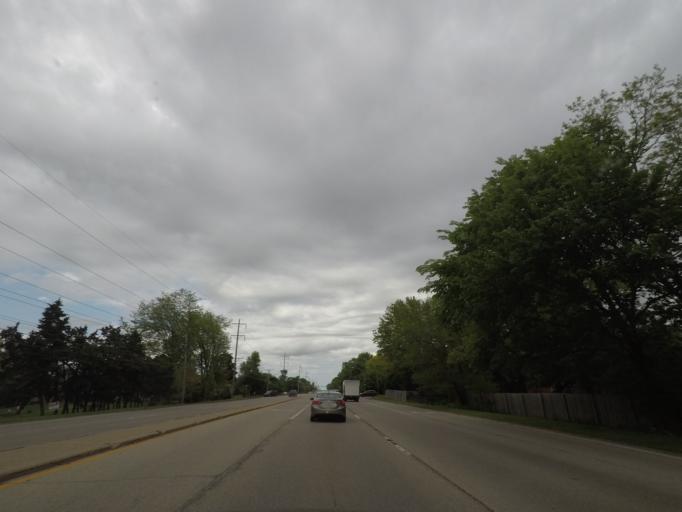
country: US
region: Illinois
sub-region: Winnebago County
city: Loves Park
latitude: 42.3032
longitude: -89.0291
